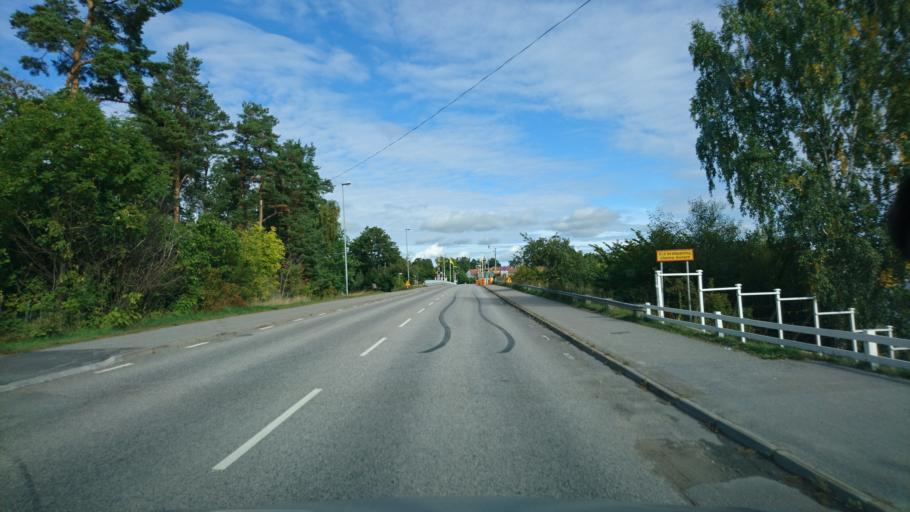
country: SE
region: Soedermanland
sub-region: Strangnas Kommun
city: Stallarholmen
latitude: 59.3633
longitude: 17.2049
